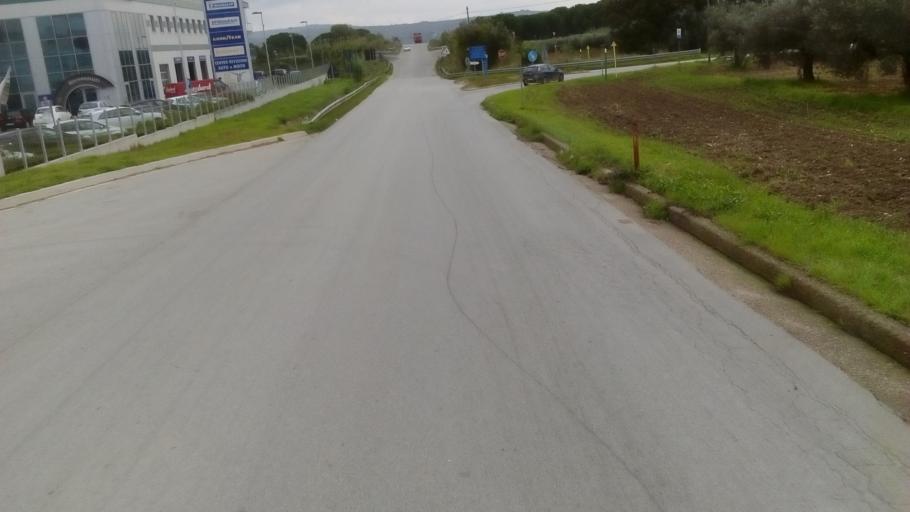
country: IT
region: Abruzzo
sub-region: Provincia di Chieti
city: San Salvo
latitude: 42.0329
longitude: 14.7421
